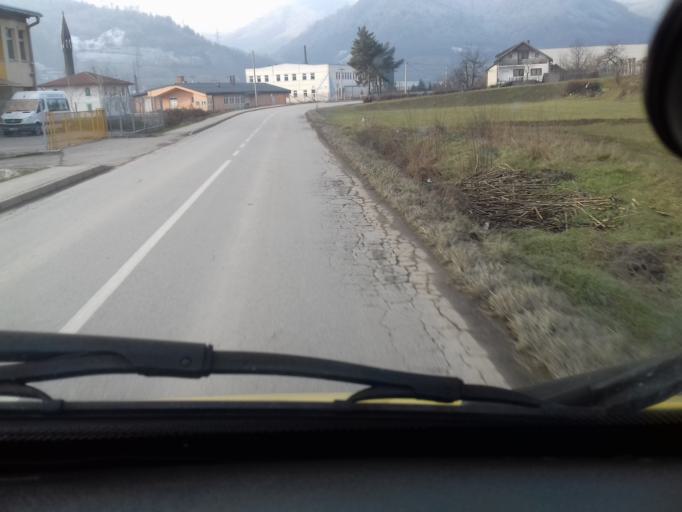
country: BA
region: Federation of Bosnia and Herzegovina
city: Dobrinje
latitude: 44.0506
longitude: 18.1102
